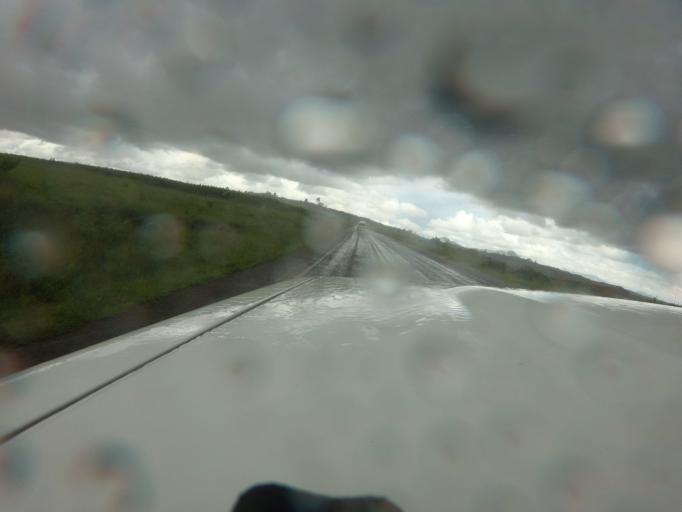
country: MW
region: Central Region
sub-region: Dedza District
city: Dedza
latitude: -14.3972
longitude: 34.3792
